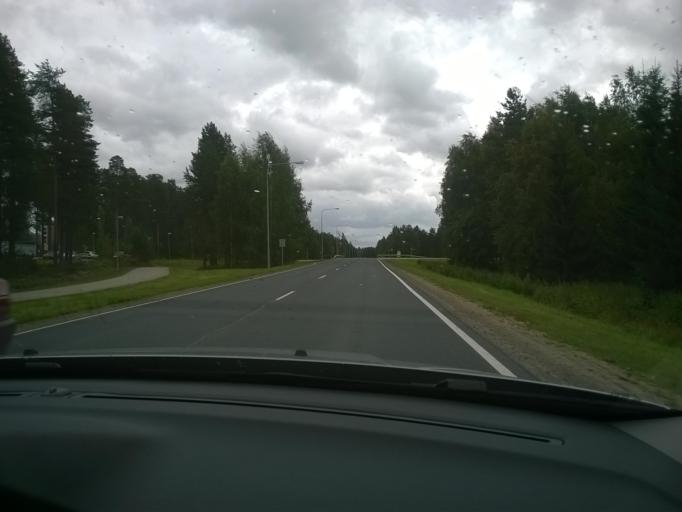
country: FI
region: Kainuu
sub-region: Kehys-Kainuu
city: Kuhmo
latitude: 64.1210
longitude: 29.5139
